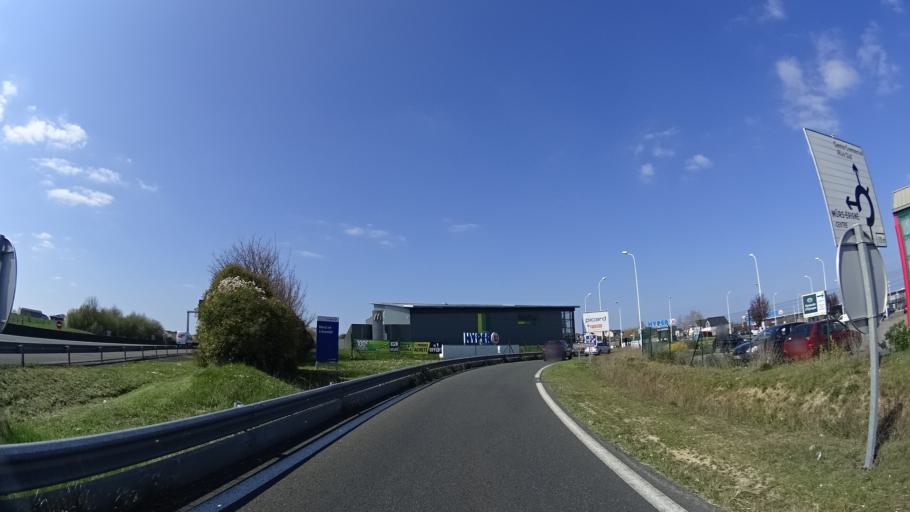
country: FR
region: Pays de la Loire
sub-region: Departement de Maine-et-Loire
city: Murs-Erigne
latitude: 47.3958
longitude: -0.5277
